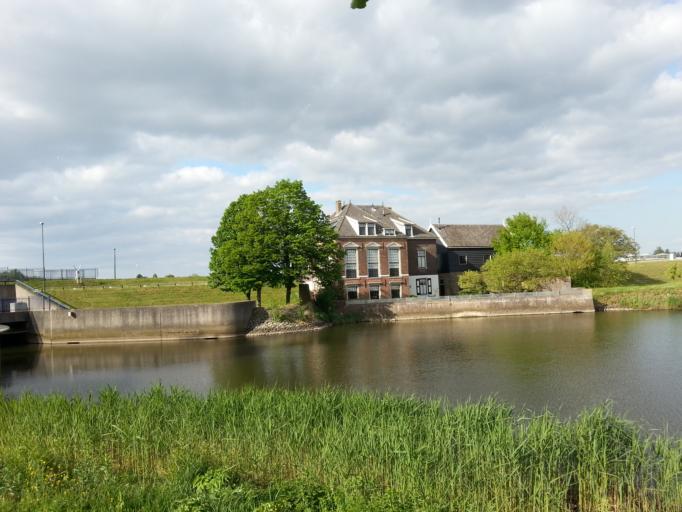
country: NL
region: South Holland
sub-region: Gemeente Alblasserdam
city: Alblasserdam
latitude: 51.8889
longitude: 4.6368
